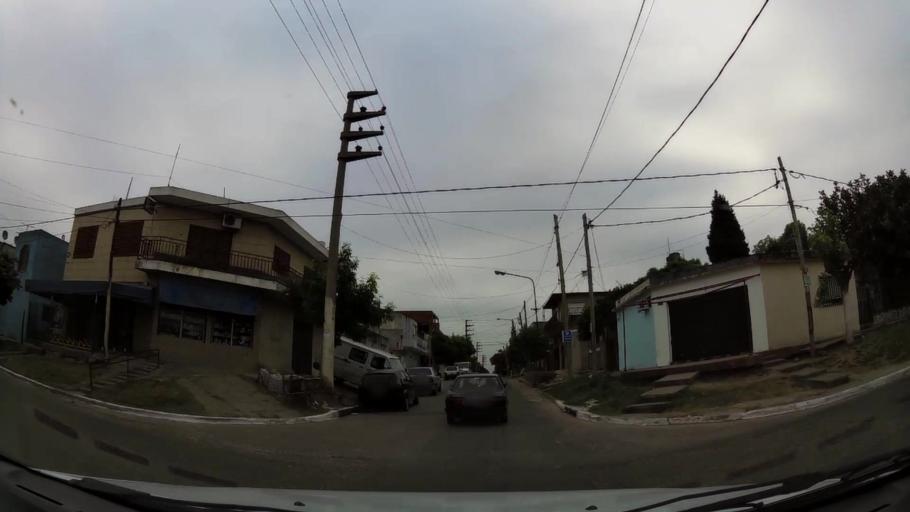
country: AR
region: Buenos Aires
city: San Justo
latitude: -34.7034
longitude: -58.5688
